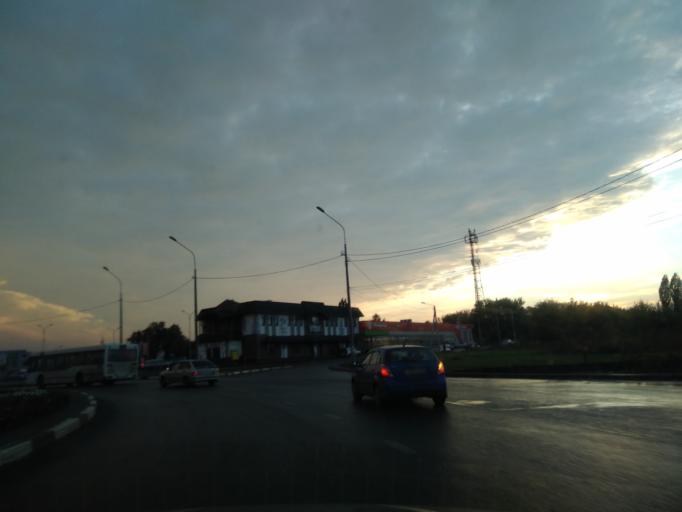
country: RU
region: Lipetsk
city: Syrskoye
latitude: 52.5714
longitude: 39.5146
